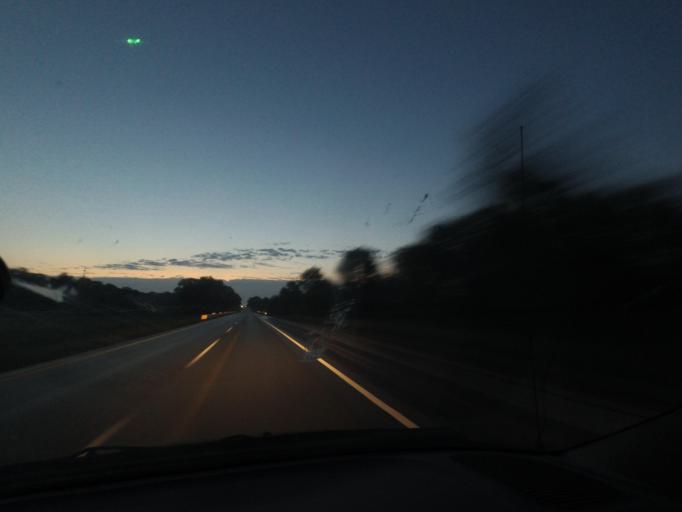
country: US
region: Missouri
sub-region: Linn County
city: Linneus
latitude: 39.7774
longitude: -93.3138
